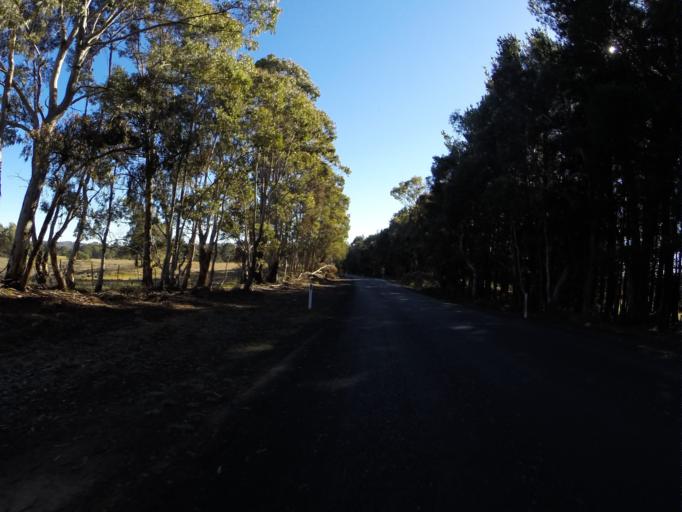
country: AU
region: New South Wales
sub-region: Oberon
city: Oberon
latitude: -33.6398
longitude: 149.8475
